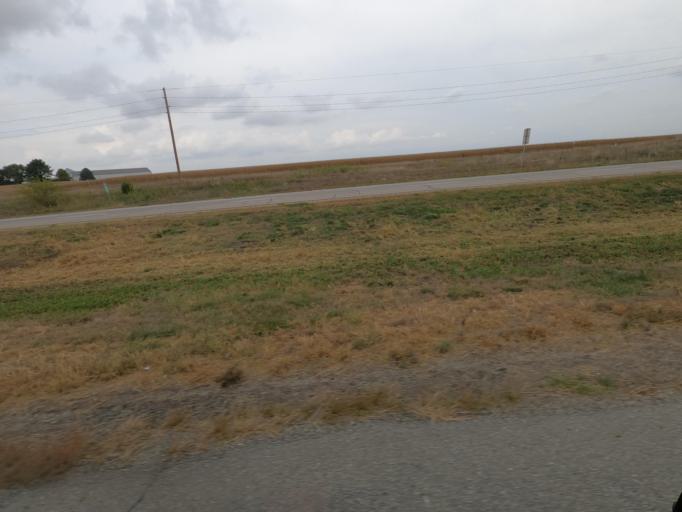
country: US
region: Iowa
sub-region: Jasper County
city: Monroe
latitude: 41.5530
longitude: -93.1393
